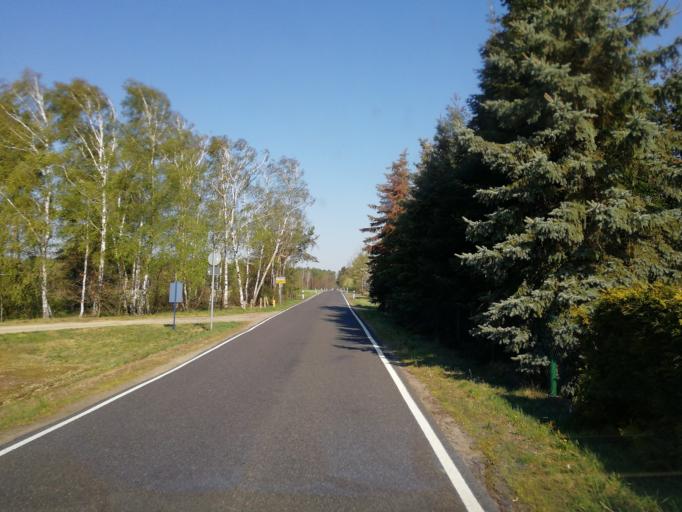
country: DE
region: Brandenburg
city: Bronkow
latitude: 51.7049
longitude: 13.8762
